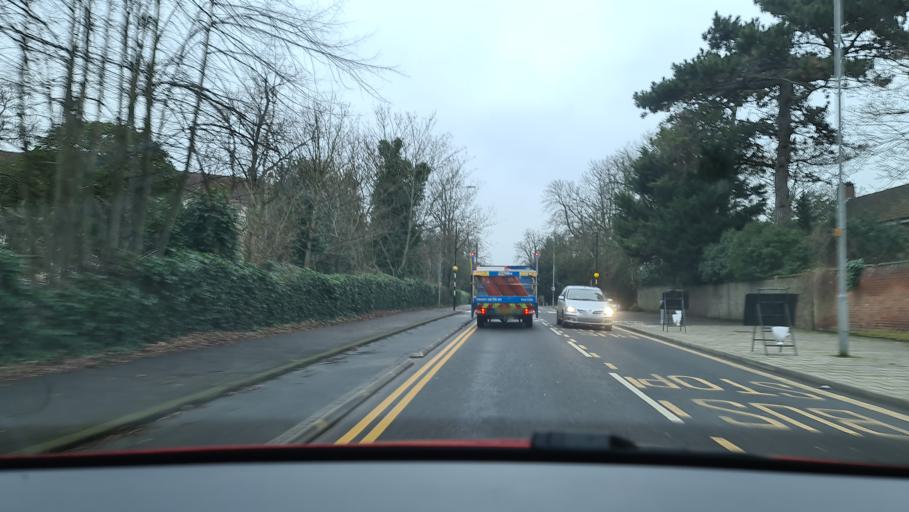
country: GB
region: England
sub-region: Greater London
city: Kingston upon Thames
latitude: 51.4213
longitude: -0.2775
